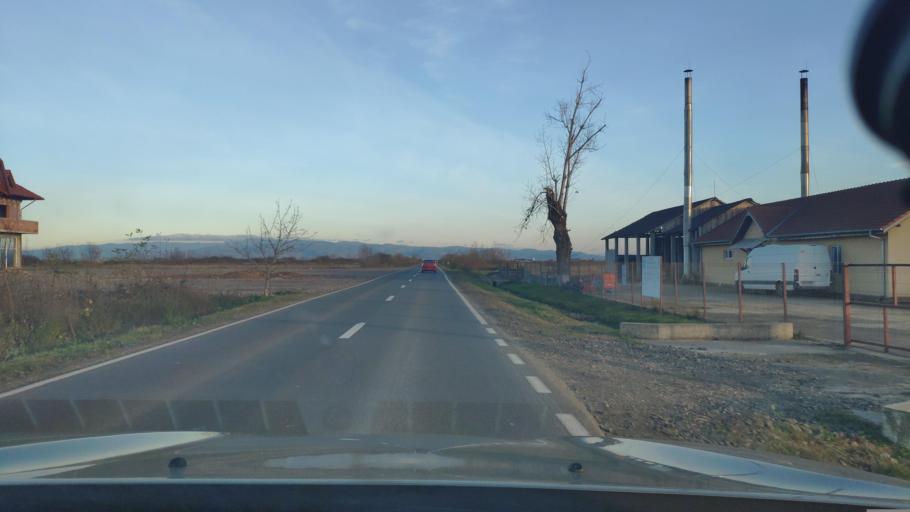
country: RO
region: Satu Mare
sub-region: Comuna Mediesu Aurit
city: Potau
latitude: 47.7726
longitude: 23.1284
